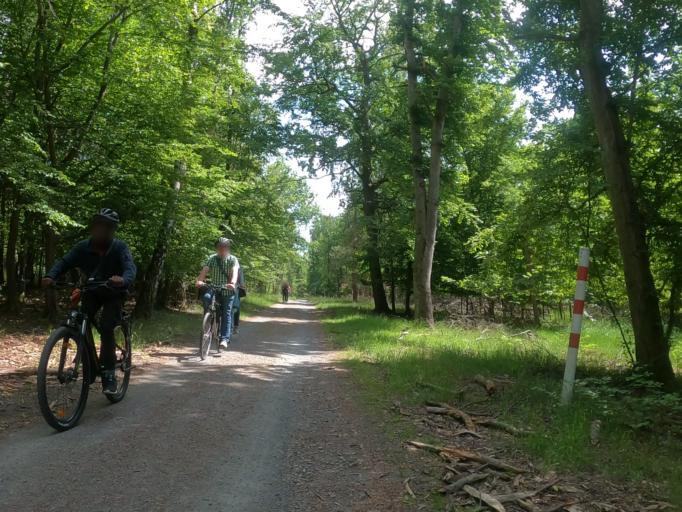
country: DE
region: Hesse
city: Morfelden-Walldorf
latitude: 49.9813
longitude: 8.5424
